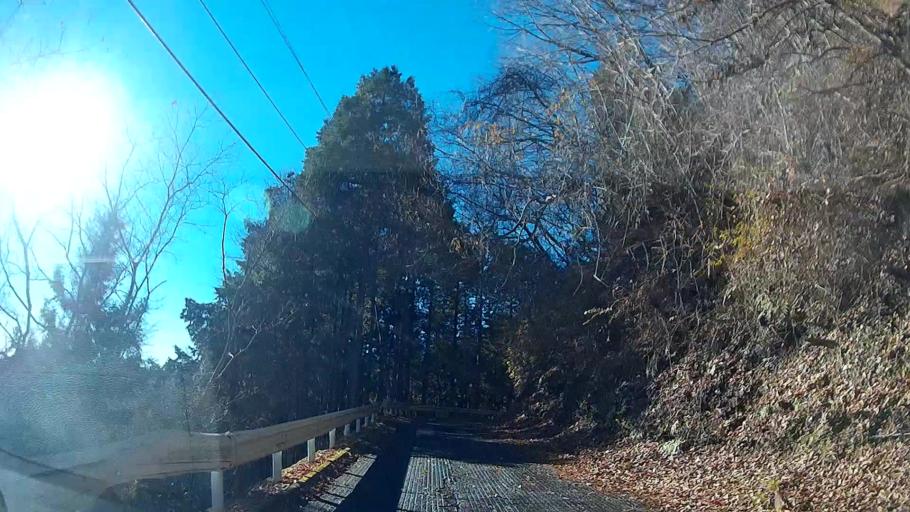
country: JP
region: Saitama
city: Chichibu
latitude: 35.9434
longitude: 139.1629
